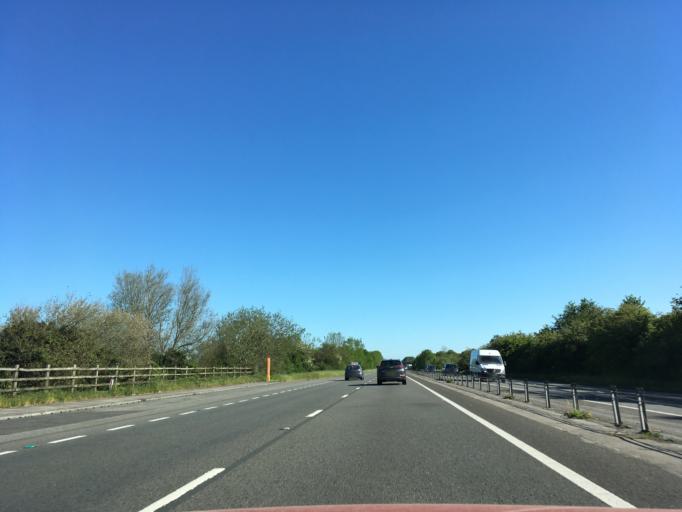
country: GB
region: Wales
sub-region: Monmouthshire
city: Llangwm
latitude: 51.7397
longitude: -2.8413
